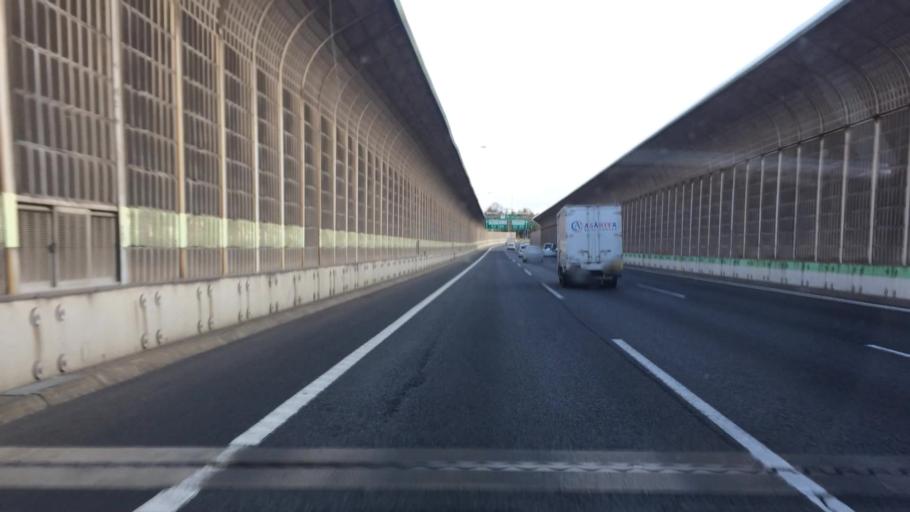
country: JP
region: Chiba
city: Chiba
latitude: 35.6508
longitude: 140.0888
